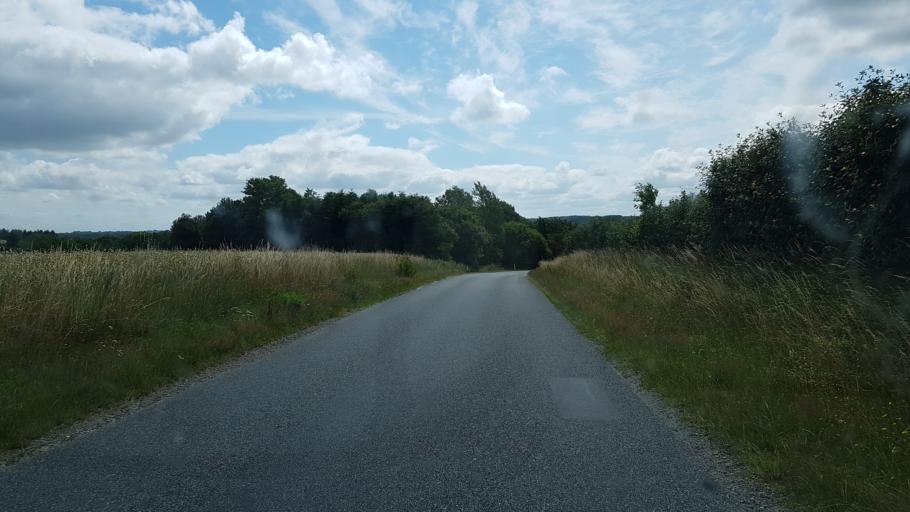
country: DK
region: South Denmark
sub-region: Vejen Kommune
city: Brorup
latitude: 55.4516
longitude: 8.9958
